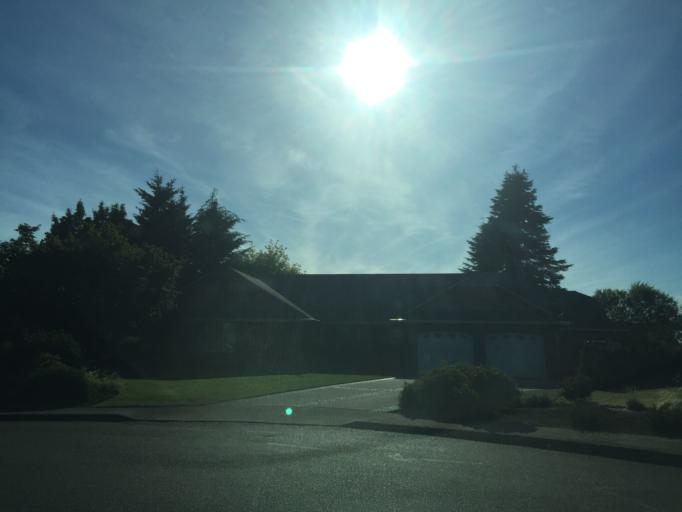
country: US
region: Washington
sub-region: Whatcom County
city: Lynden
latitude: 48.9451
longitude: -122.4710
